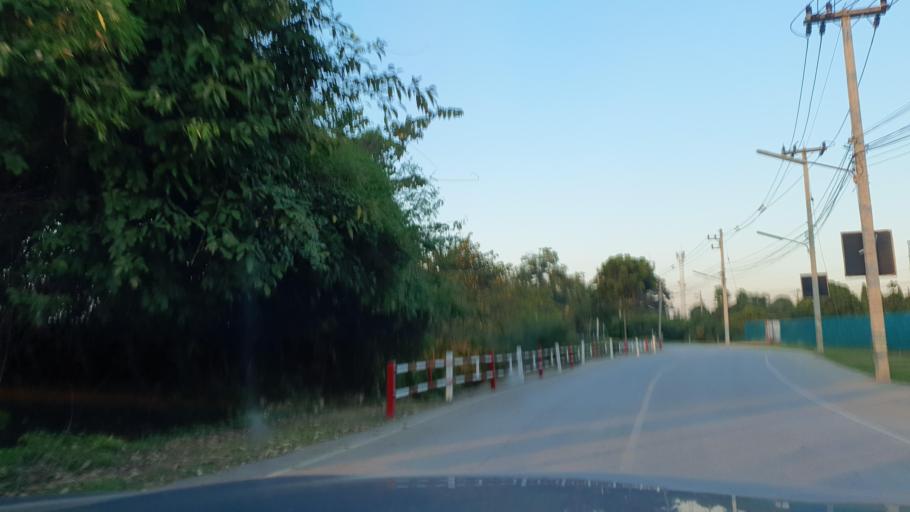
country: TH
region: Chiang Mai
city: Saraphi
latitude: 18.7337
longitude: 99.0723
